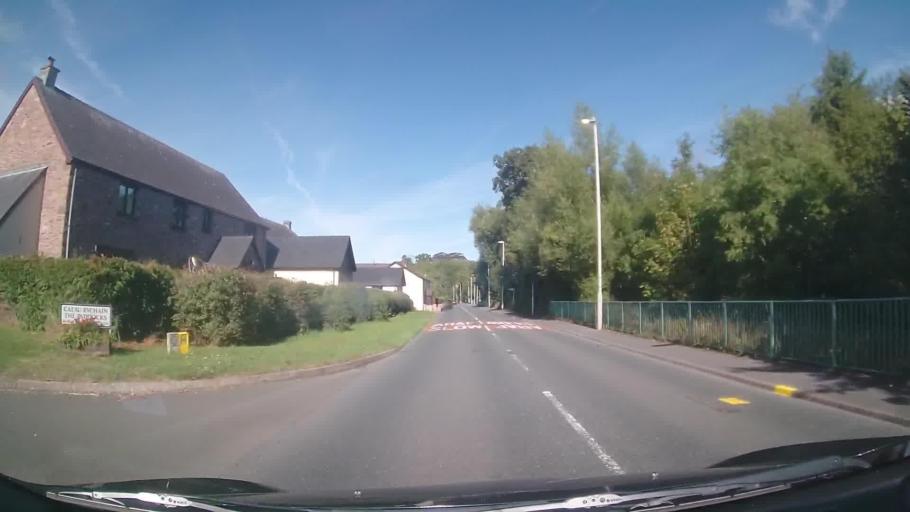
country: GB
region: Wales
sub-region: Sir Powys
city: Hay
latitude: 52.0008
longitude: -3.2364
